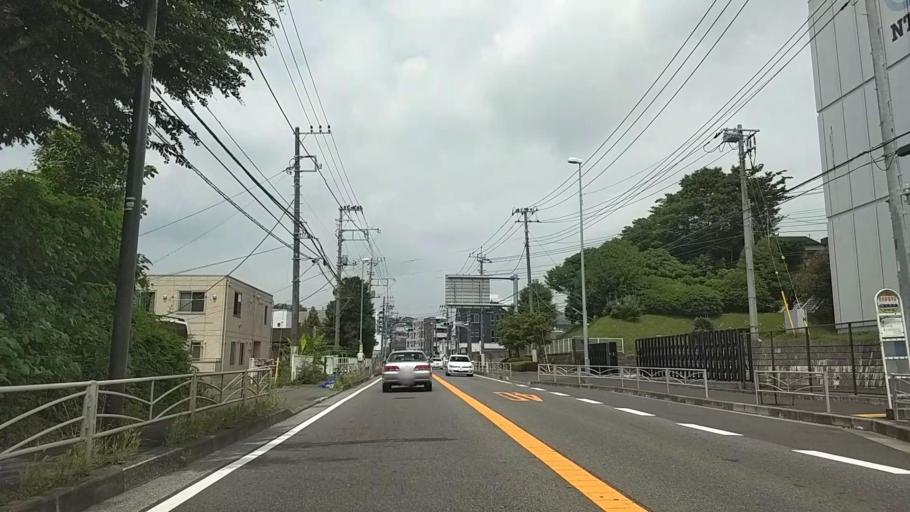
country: JP
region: Kanagawa
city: Yokohama
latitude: 35.4753
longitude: 139.5724
